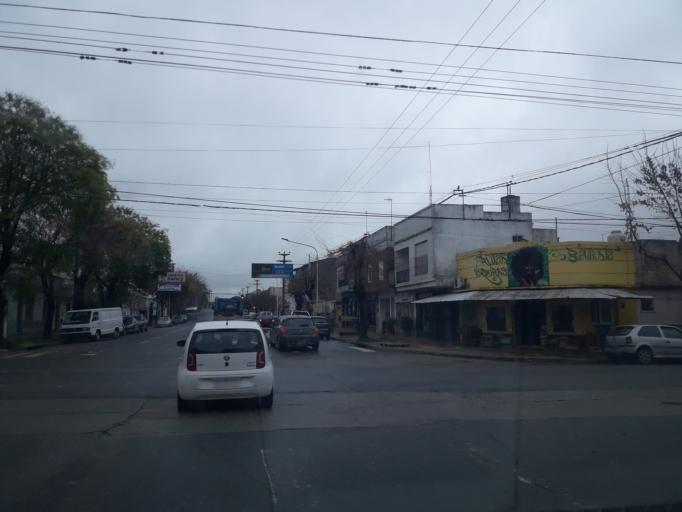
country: AR
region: Buenos Aires
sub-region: Partido de Tandil
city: Tandil
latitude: -37.3201
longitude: -59.1506
